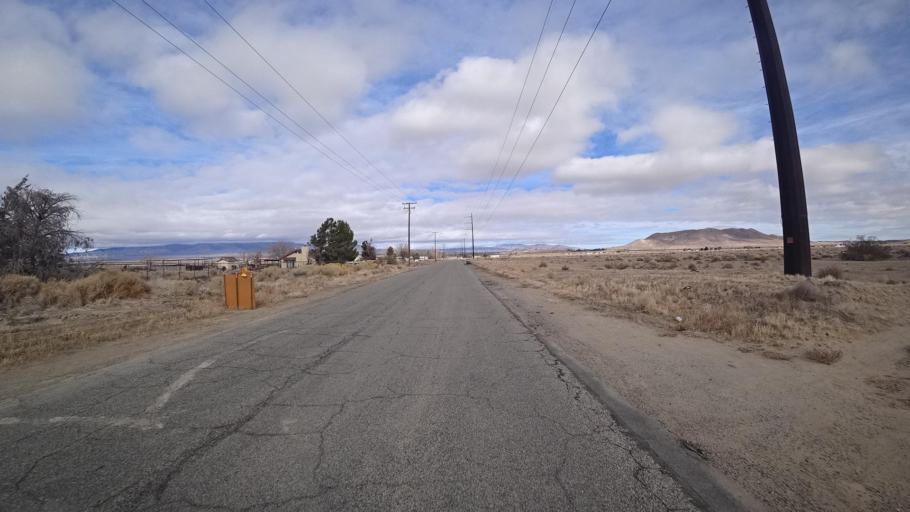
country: US
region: California
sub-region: Kern County
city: Rosamond
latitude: 34.8489
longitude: -118.3089
